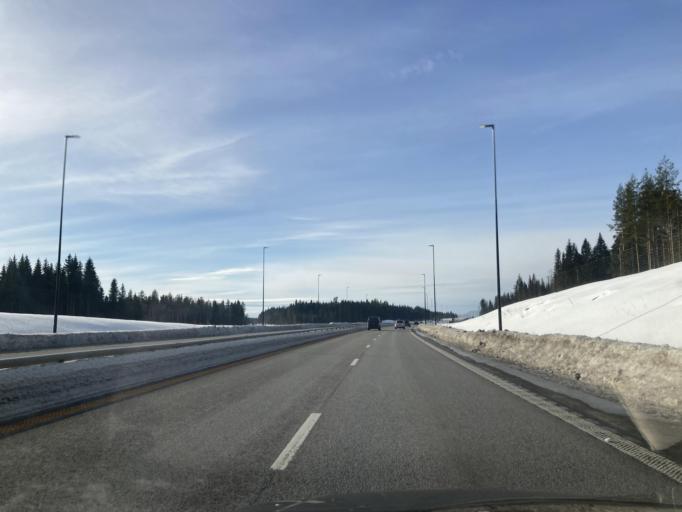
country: NO
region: Hedmark
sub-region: Loten
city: Loten
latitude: 60.8673
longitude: 11.4350
